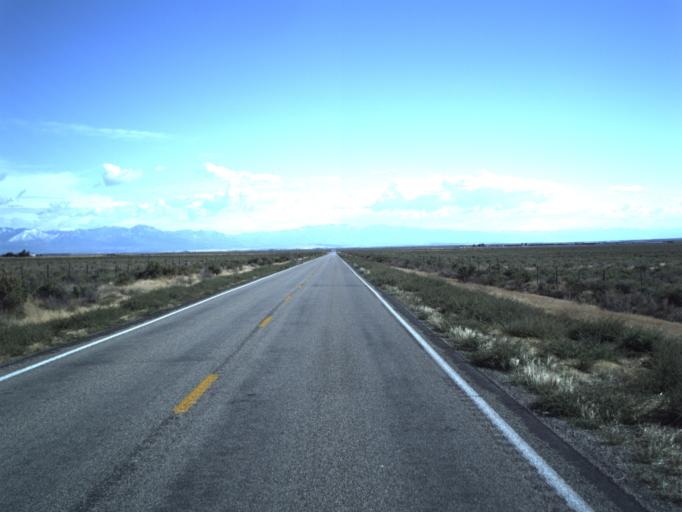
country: US
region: Utah
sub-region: Millard County
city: Delta
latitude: 39.3445
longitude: -112.4942
